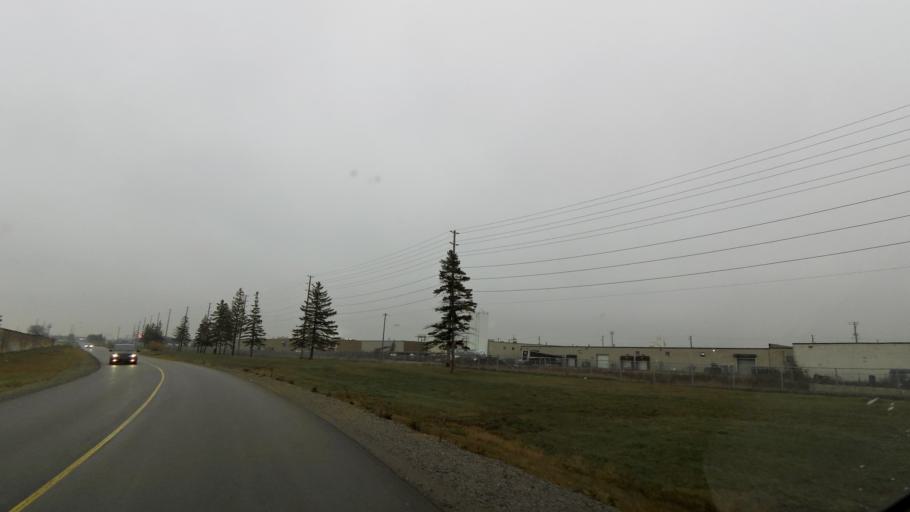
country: CA
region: Ontario
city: Etobicoke
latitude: 43.7060
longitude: -79.6103
